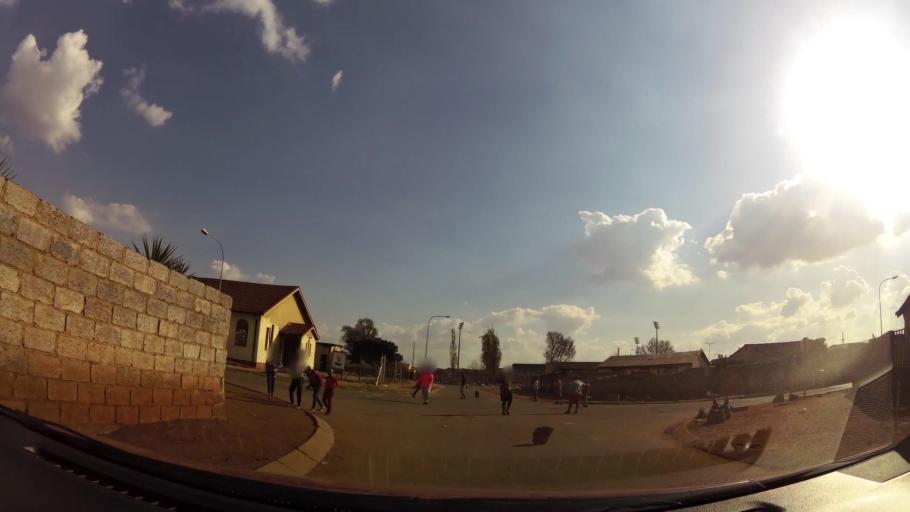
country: ZA
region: Gauteng
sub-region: City of Johannesburg Metropolitan Municipality
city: Soweto
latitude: -26.2269
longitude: 27.8684
